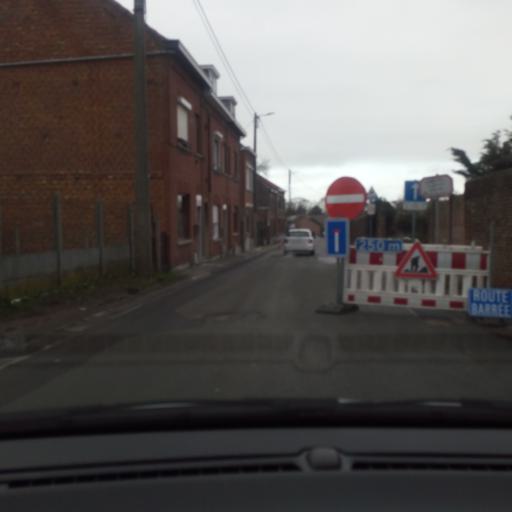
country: BE
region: Wallonia
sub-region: Province du Hainaut
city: Dour
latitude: 50.3951
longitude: 3.7760
